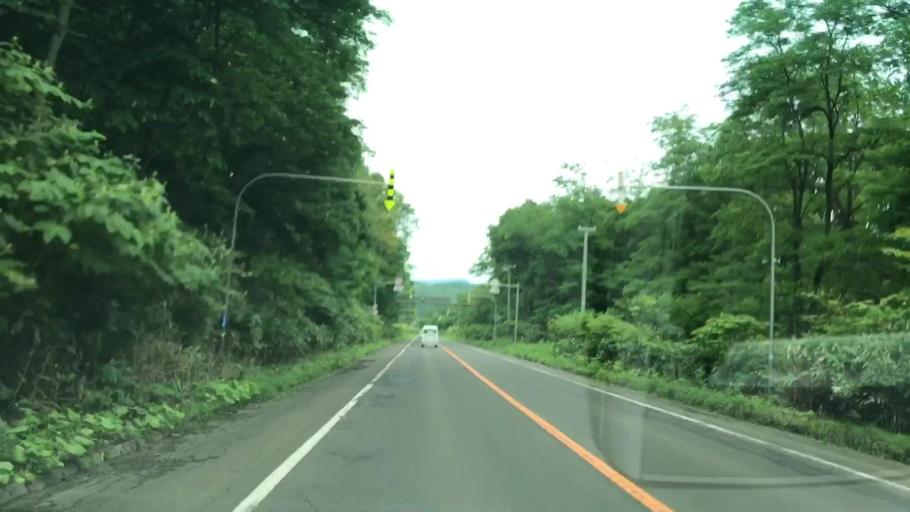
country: JP
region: Hokkaido
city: Niseko Town
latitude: 42.9537
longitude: 140.6971
